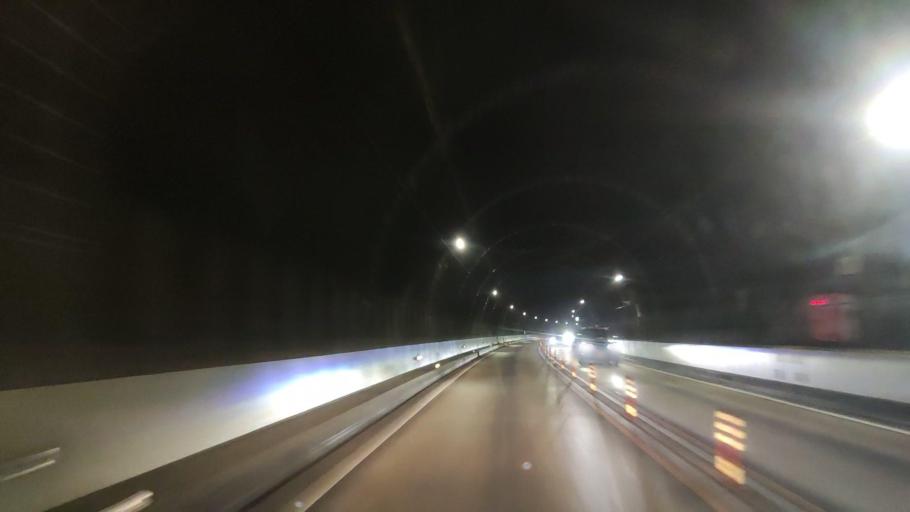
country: JP
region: Hiroshima
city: Innoshima
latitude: 34.1829
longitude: 133.0687
